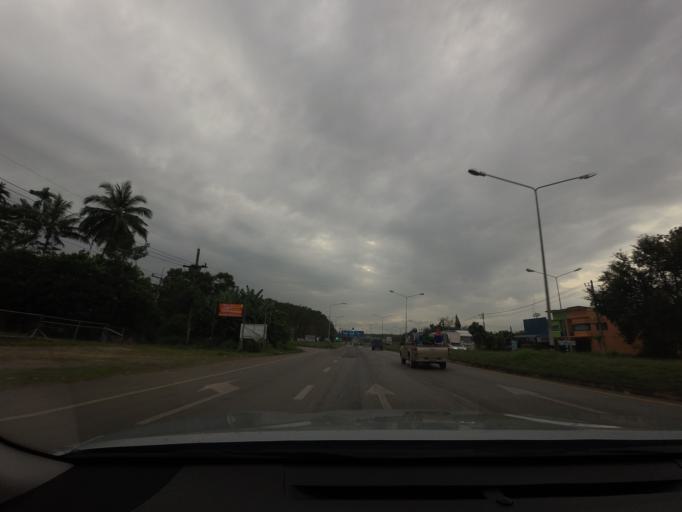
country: TH
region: Surat Thani
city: Phunphin
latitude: 9.0496
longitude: 99.1629
